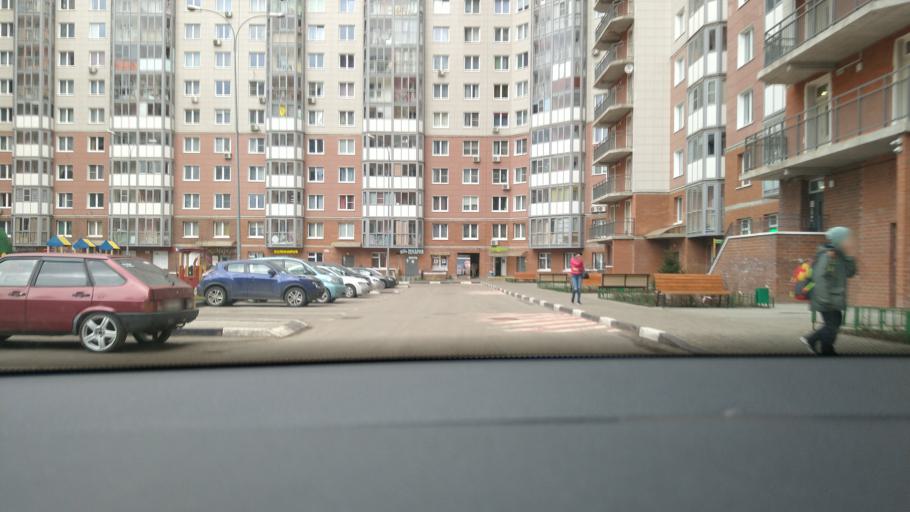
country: RU
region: Moskovskaya
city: Opalikha
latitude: 55.8355
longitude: 37.2770
